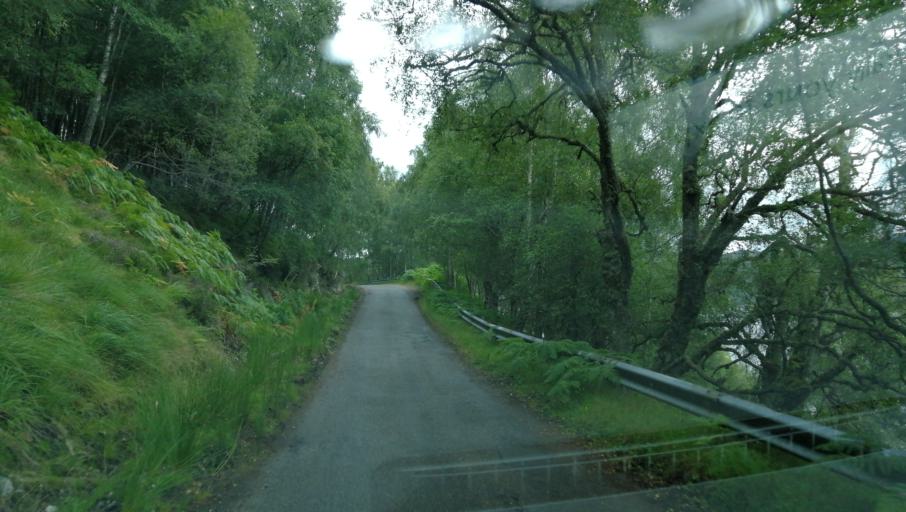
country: GB
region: Scotland
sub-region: Highland
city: Spean Bridge
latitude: 57.2762
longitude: -4.9485
